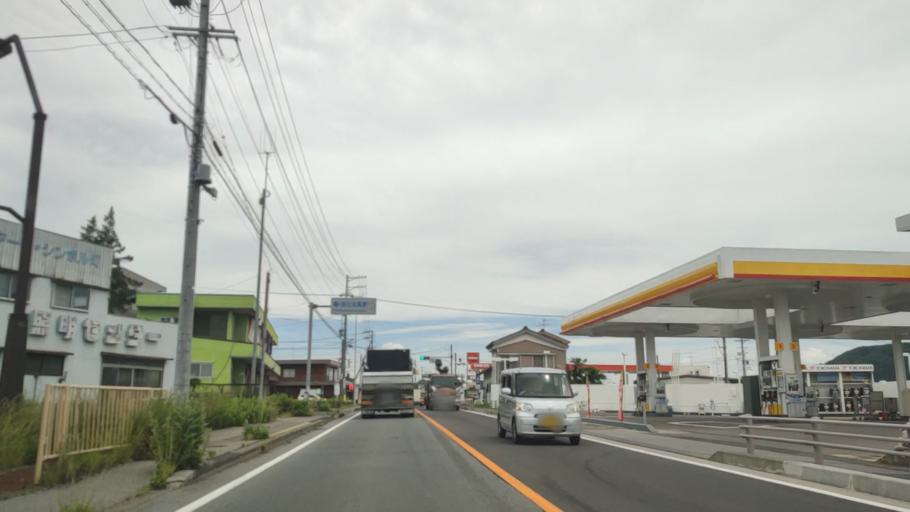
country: JP
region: Nagano
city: Komoro
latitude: 36.3489
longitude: 138.3647
